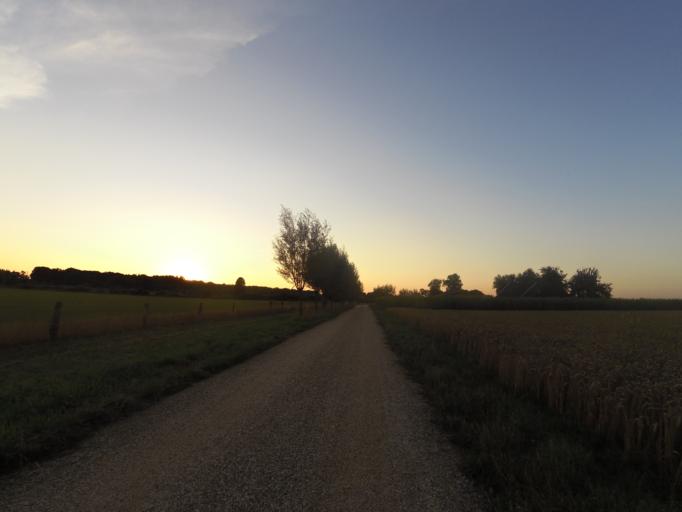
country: NL
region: Gelderland
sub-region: Oude IJsselstreek
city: Gendringen
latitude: 51.8730
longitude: 6.4061
